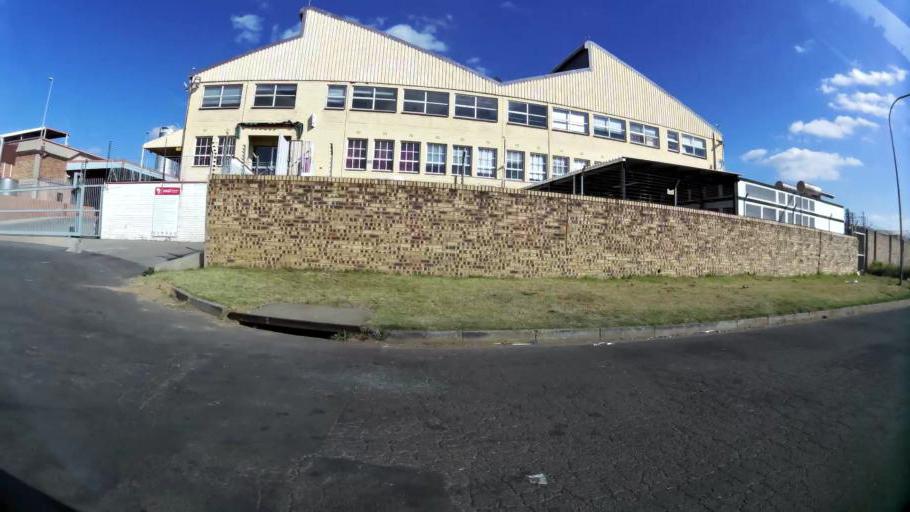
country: ZA
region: Gauteng
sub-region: City of Johannesburg Metropolitan Municipality
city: Soweto
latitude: -26.2719
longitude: 27.9410
